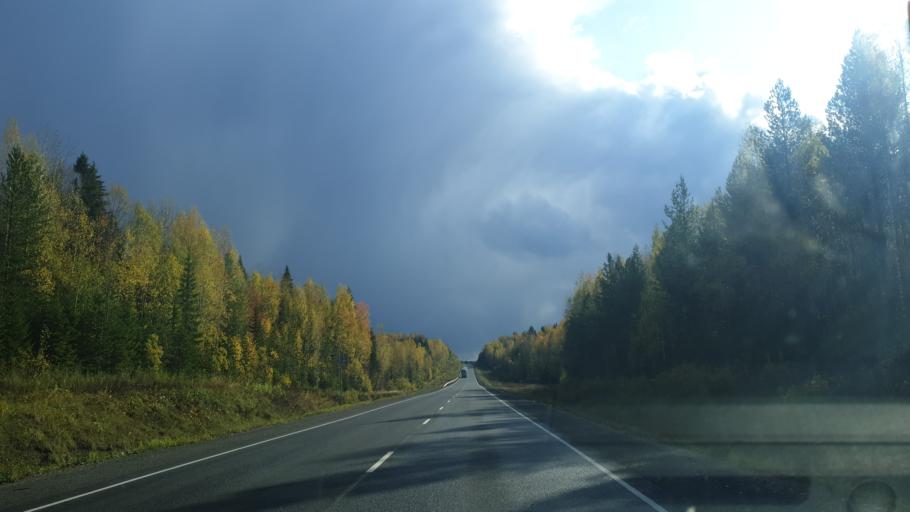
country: RU
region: Komi Republic
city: Vizinga
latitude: 60.7292
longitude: 49.4966
